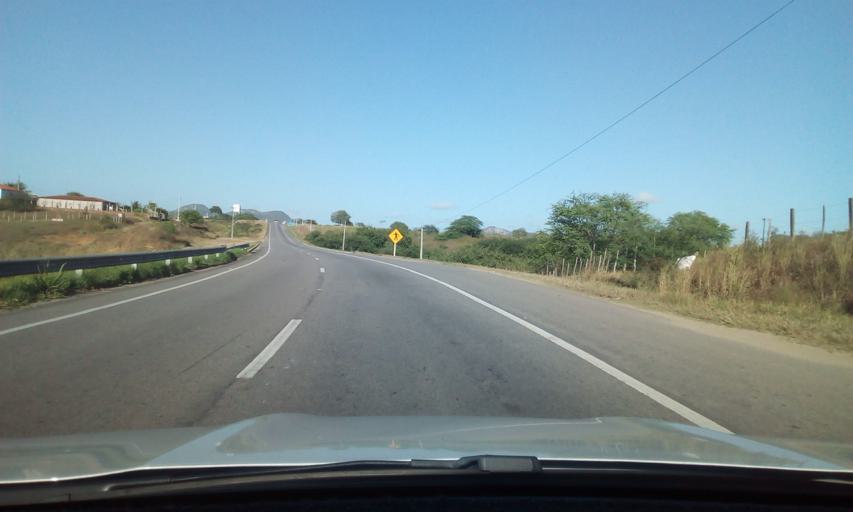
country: BR
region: Paraiba
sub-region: Gurinhem
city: Gurinhem
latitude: -7.1629
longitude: -35.3477
